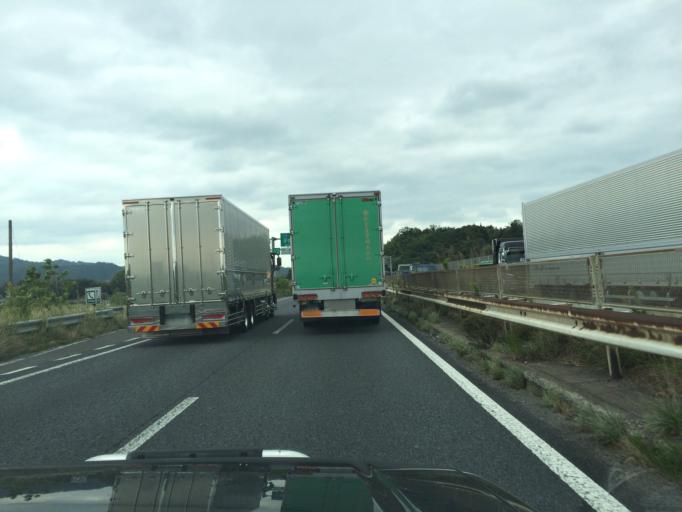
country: JP
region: Mie
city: Ueno-ebisumachi
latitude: 34.7805
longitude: 136.1584
